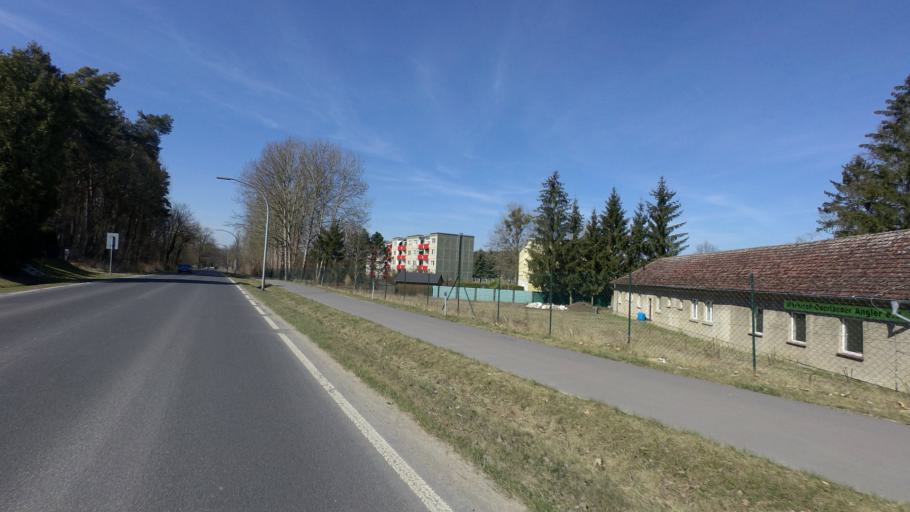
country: DE
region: Brandenburg
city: Muncheberg
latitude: 52.5162
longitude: 14.1123
